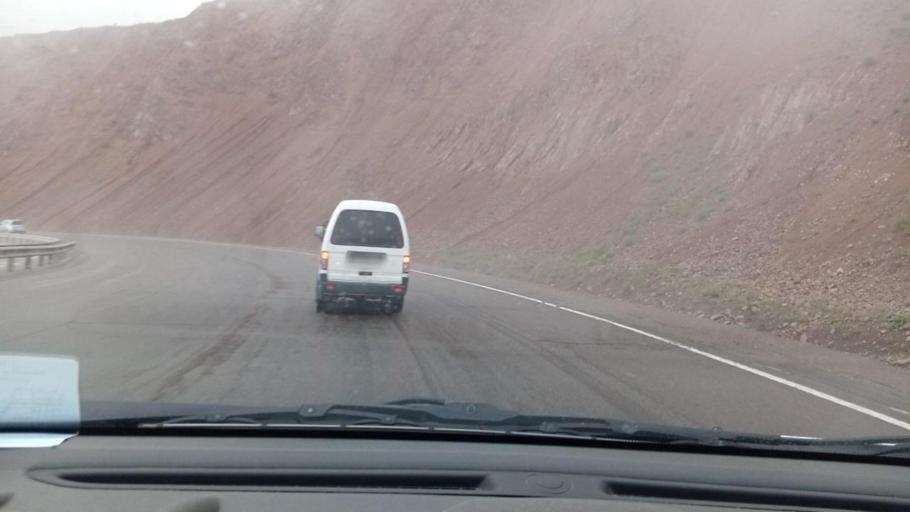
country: UZ
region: Toshkent
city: Angren
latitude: 41.1122
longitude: 70.5058
